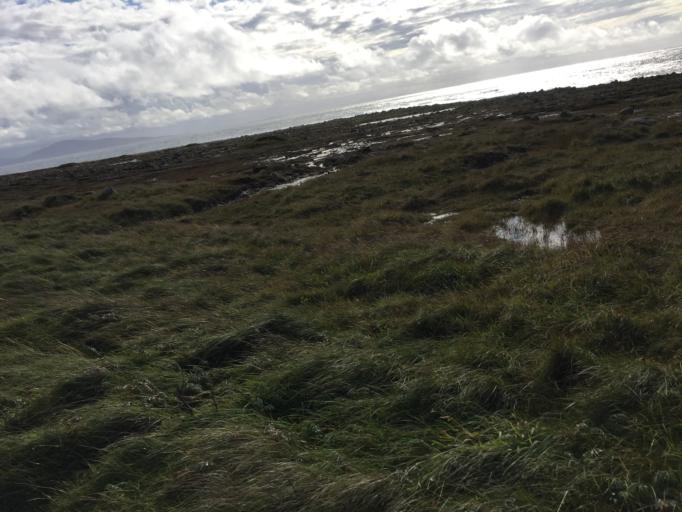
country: IE
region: Ulster
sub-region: County Donegal
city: Derrybeg
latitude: 55.2708
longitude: -8.2485
